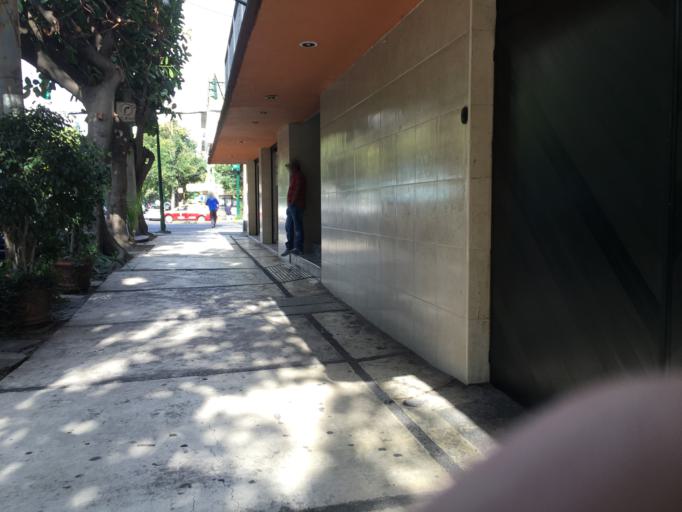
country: MX
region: Mexico City
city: Colonia del Valle
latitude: 19.3737
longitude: -99.1542
